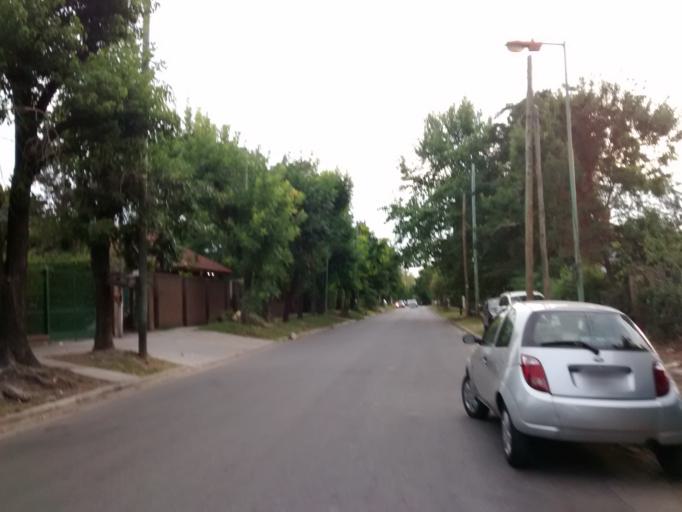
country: AR
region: Buenos Aires
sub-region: Partido de La Plata
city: La Plata
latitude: -34.8780
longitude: -58.0622
